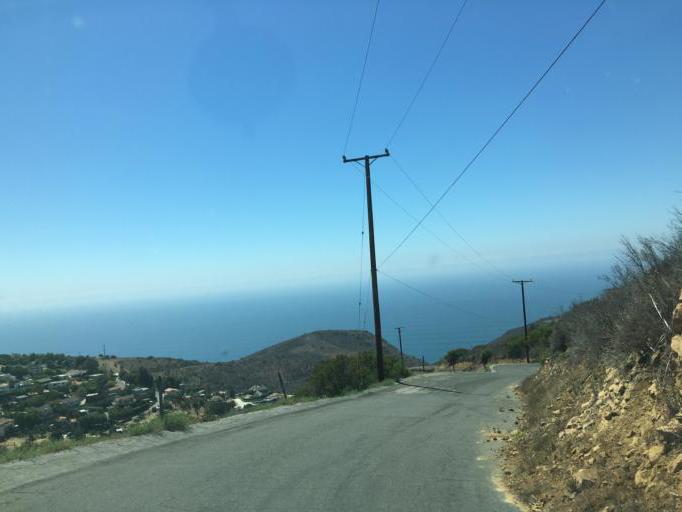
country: US
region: California
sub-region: Los Angeles County
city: Malibu Beach
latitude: 34.0486
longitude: -118.7442
